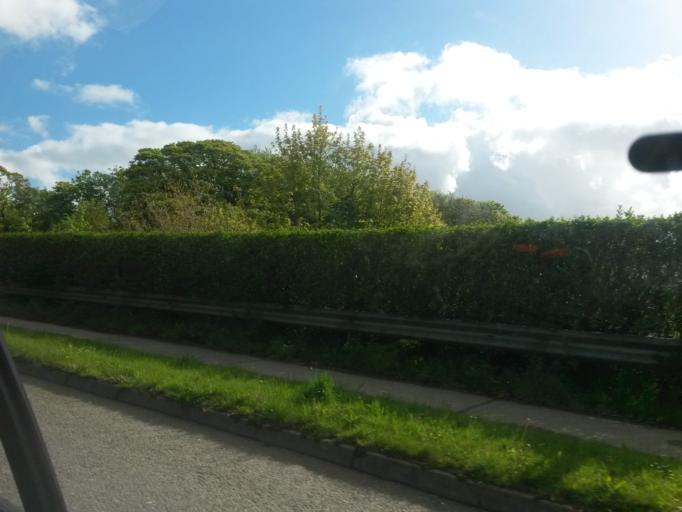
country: IE
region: Leinster
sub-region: Loch Garman
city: Enniscorthy
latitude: 52.5121
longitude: -6.5640
